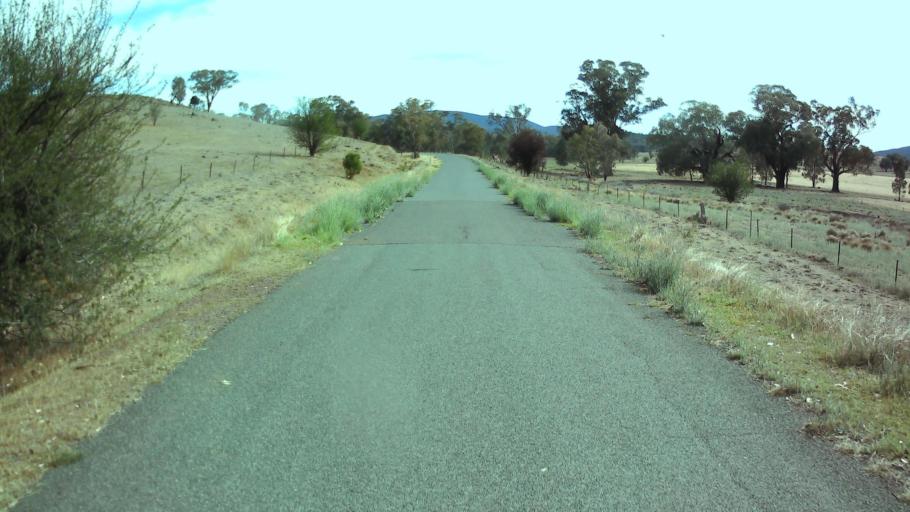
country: AU
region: New South Wales
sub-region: Weddin
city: Grenfell
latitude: -33.8190
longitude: 148.2907
